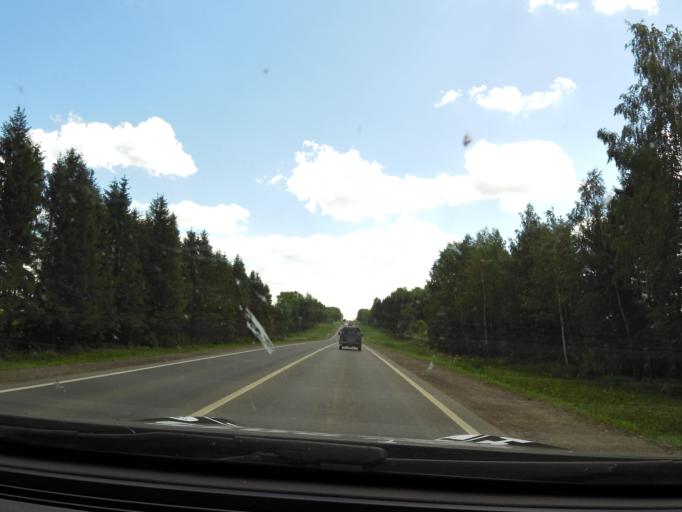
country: RU
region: Vologda
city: Molochnoye
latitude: 59.2656
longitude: 39.7379
